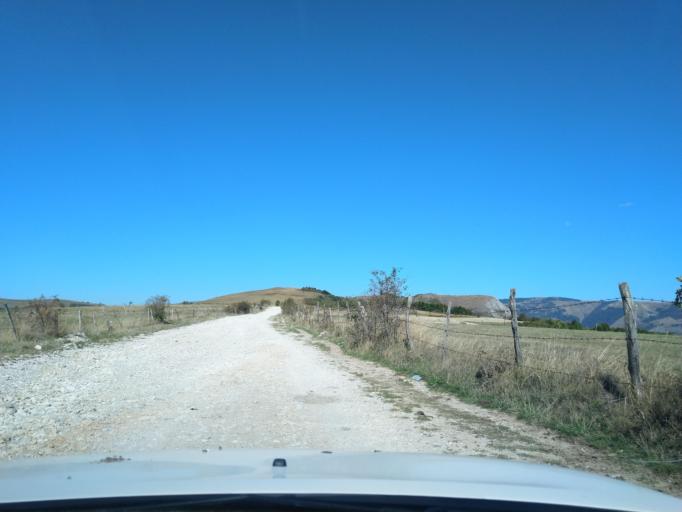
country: RS
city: Sokolovica
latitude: 43.2749
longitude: 20.2230
